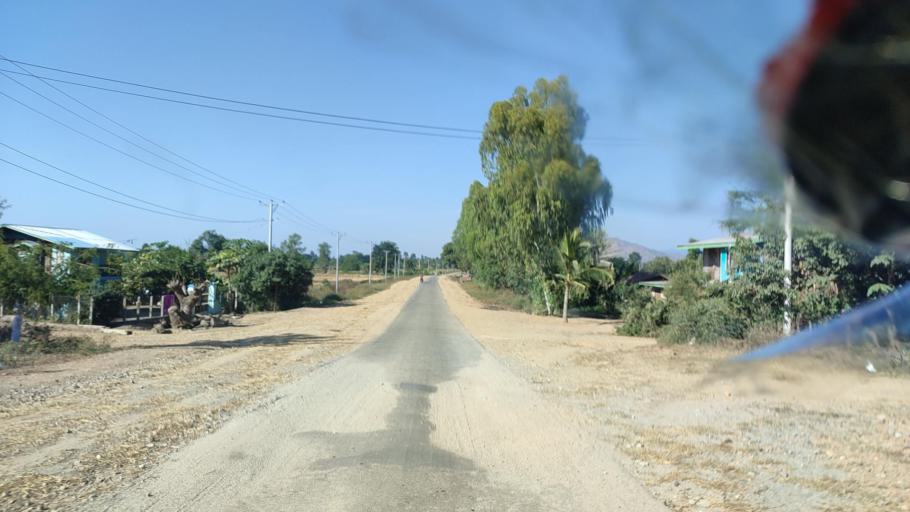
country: MM
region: Mandalay
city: Yamethin
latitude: 20.2091
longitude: 96.2633
